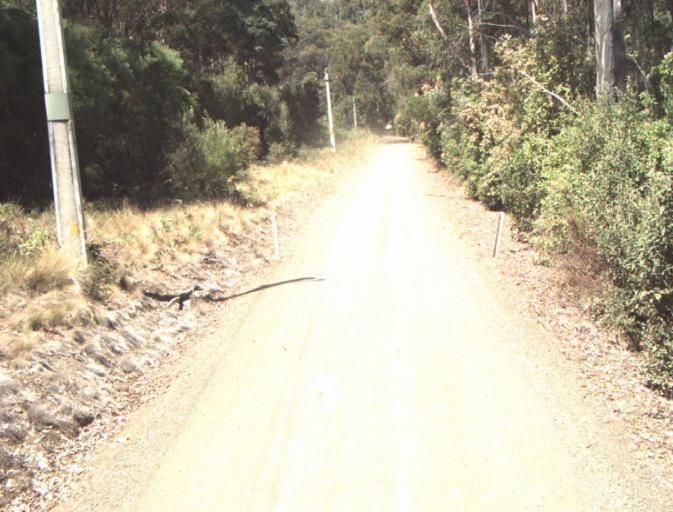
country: AU
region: Tasmania
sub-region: Dorset
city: Scottsdale
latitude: -41.3567
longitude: 147.3925
